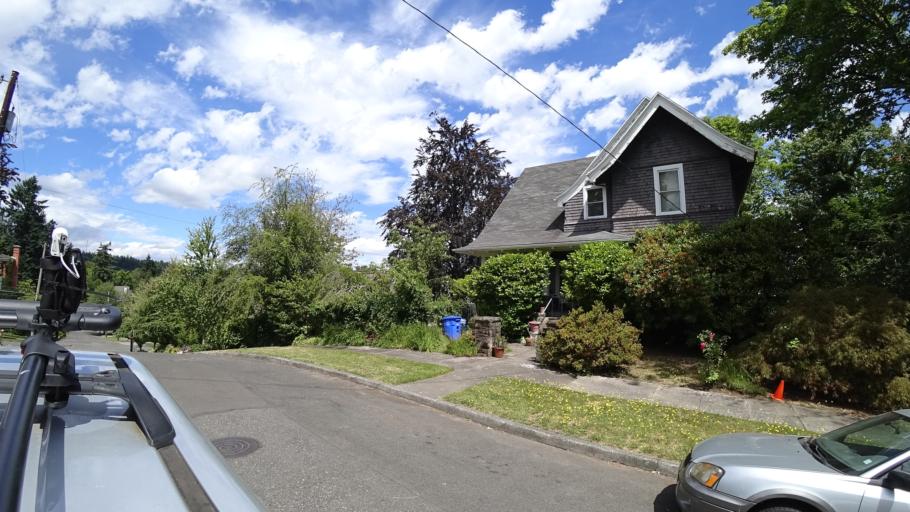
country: US
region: Oregon
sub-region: Multnomah County
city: Portland
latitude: 45.5081
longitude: -122.6946
